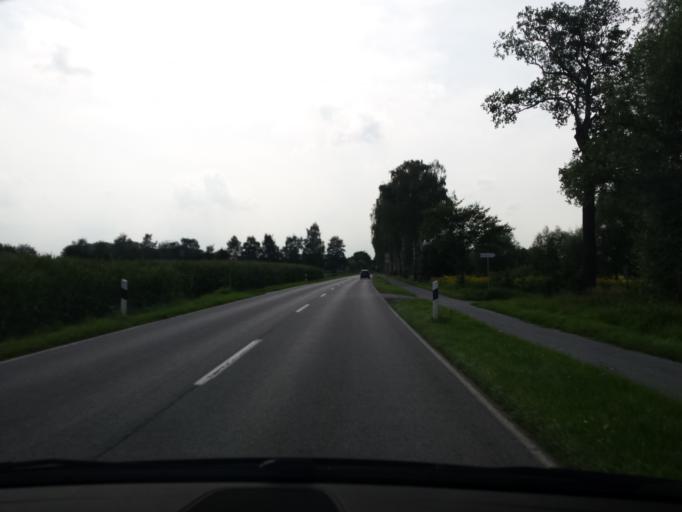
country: DE
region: North Rhine-Westphalia
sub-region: Regierungsbezirk Munster
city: Wadersloh
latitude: 51.6606
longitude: 8.2691
